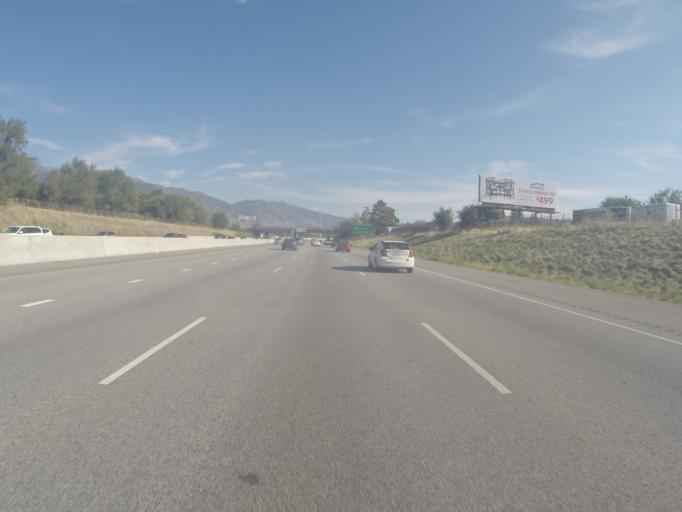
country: US
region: Utah
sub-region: Davis County
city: Layton
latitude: 41.0618
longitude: -111.9656
